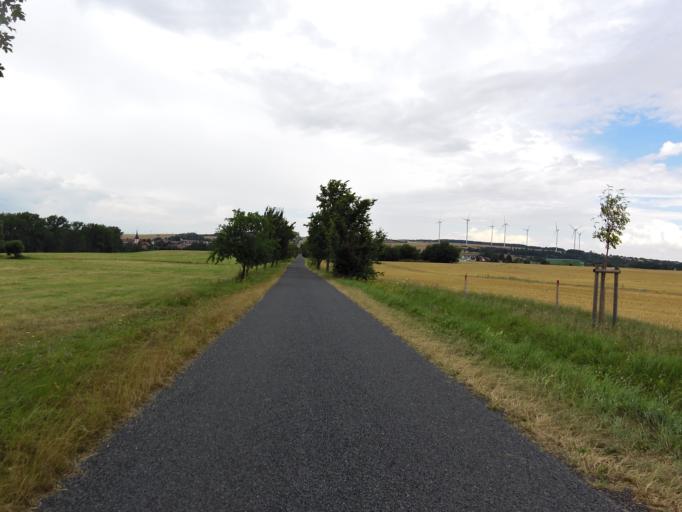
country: DE
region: Thuringia
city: Mechterstadt
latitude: 50.9324
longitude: 10.5262
